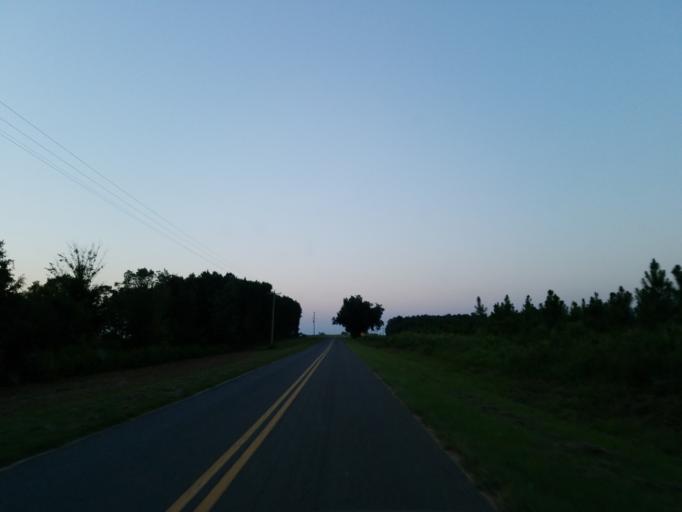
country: US
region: Georgia
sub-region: Dooly County
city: Unadilla
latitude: 32.2441
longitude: -83.7974
